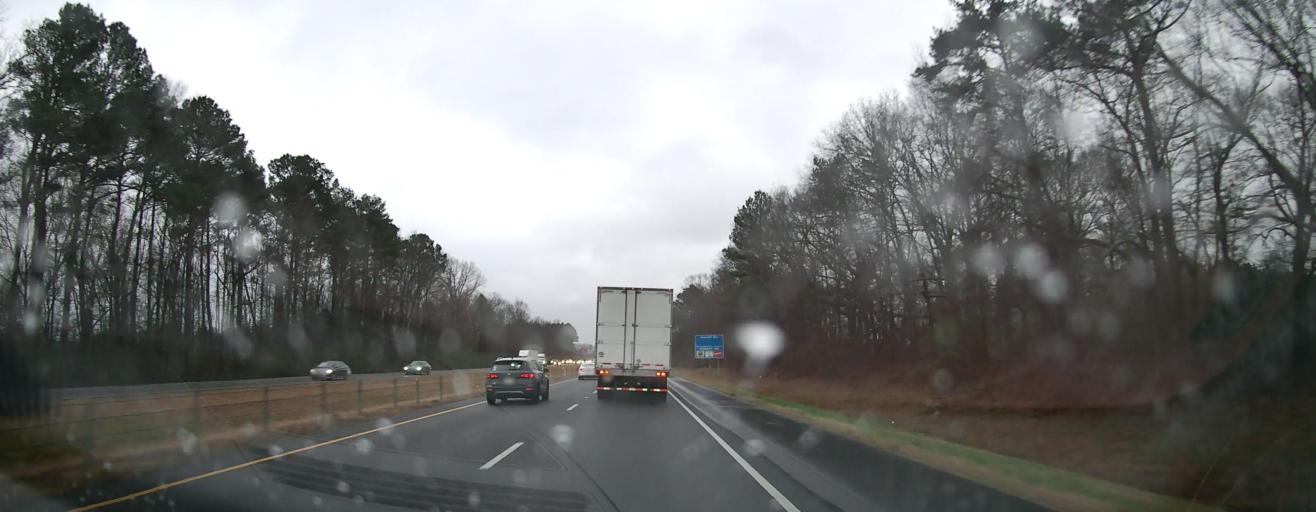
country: US
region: Alabama
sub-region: Cullman County
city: Good Hope
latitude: 34.1441
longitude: -86.8692
